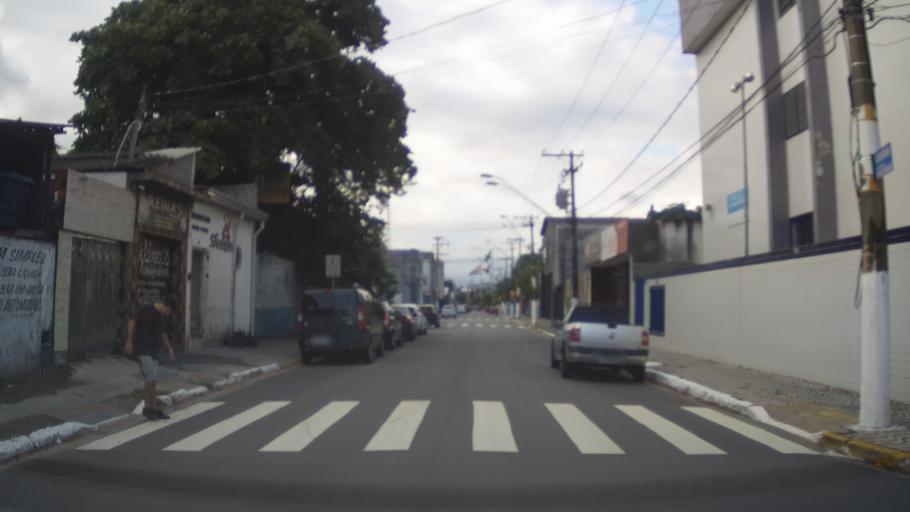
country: BR
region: Sao Paulo
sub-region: Praia Grande
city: Praia Grande
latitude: -24.0044
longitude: -46.4124
